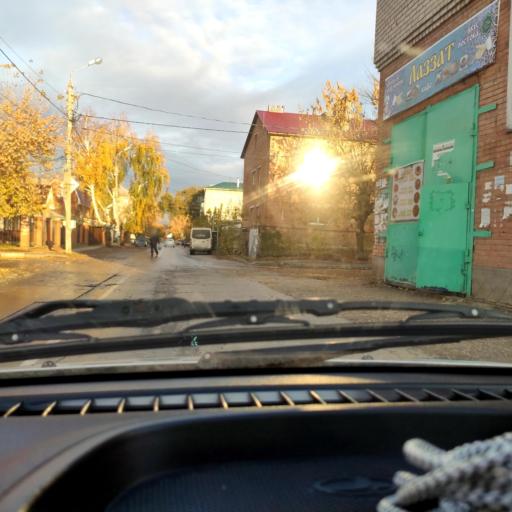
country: RU
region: Samara
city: Tol'yatti
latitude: 53.5183
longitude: 49.4086
